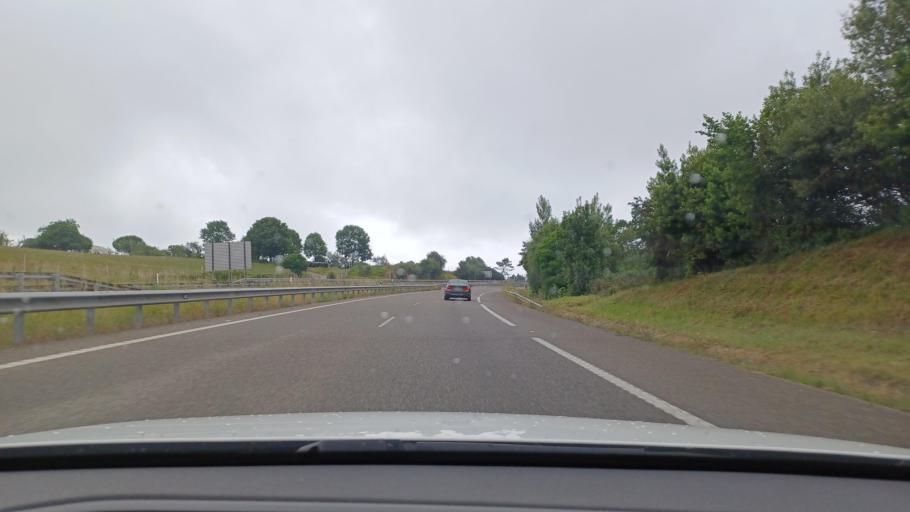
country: ES
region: Asturias
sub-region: Province of Asturias
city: Lugones
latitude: 43.4511
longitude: -5.7972
